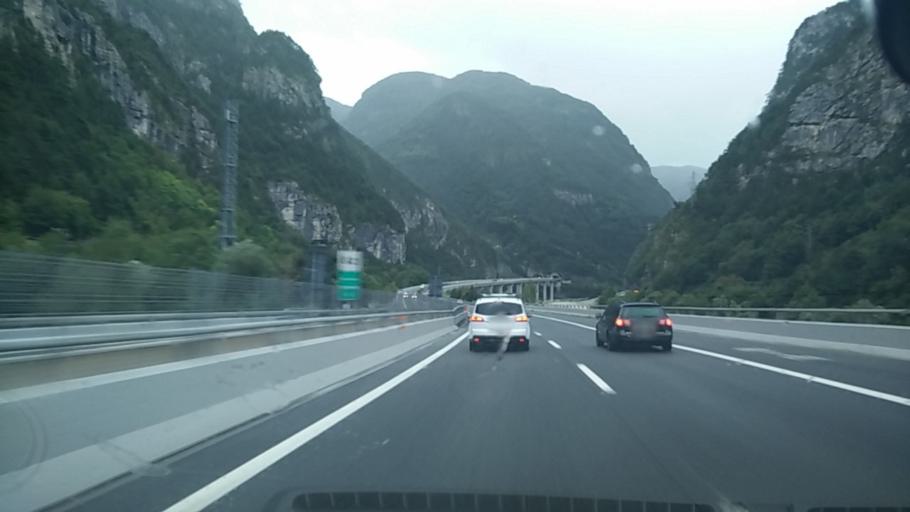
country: IT
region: Friuli Venezia Giulia
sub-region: Provincia di Udine
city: Dogna
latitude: 46.4289
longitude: 13.3160
